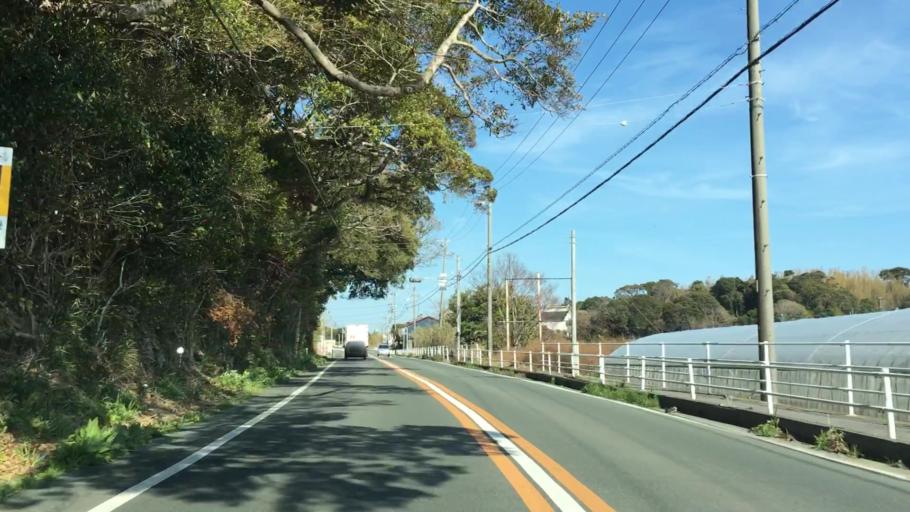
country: JP
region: Aichi
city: Toyohashi
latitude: 34.6699
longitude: 137.4139
